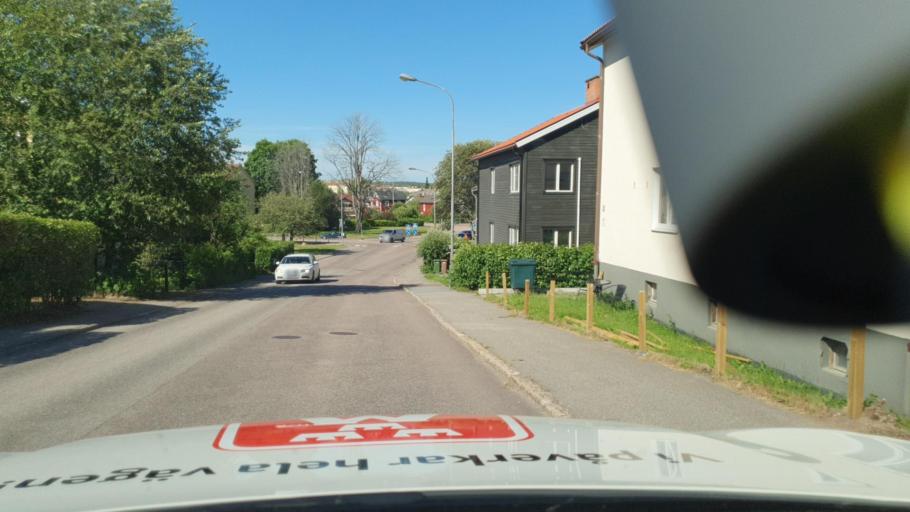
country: SE
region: Vaermland
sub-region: Kristinehamns Kommun
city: Kristinehamn
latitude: 59.3026
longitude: 14.1064
